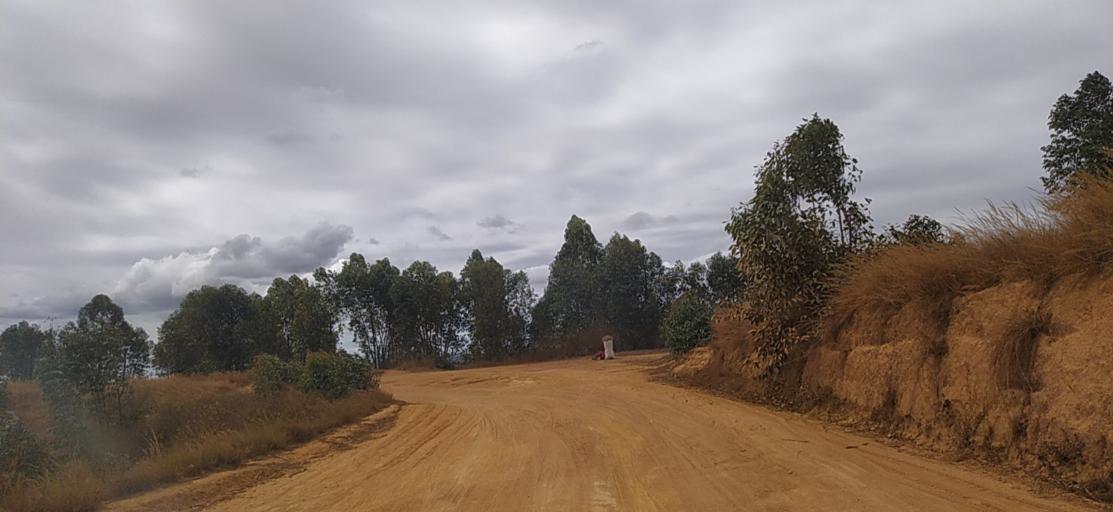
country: MG
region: Alaotra Mangoro
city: Ambatondrazaka
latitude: -17.9973
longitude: 48.2677
